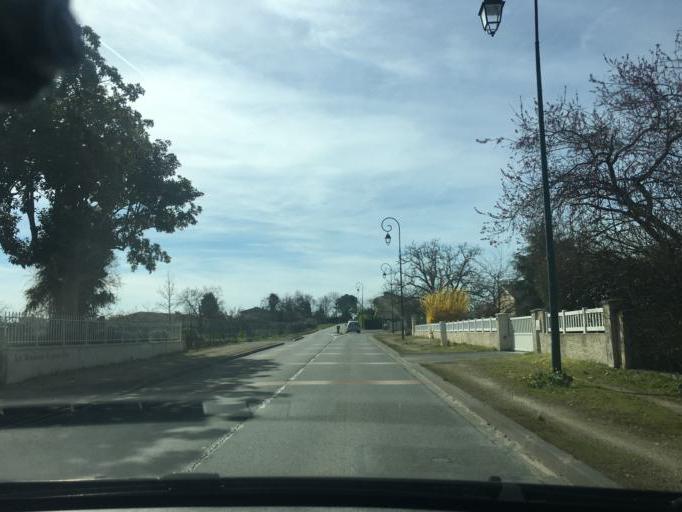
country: FR
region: Aquitaine
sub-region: Departement de la Gironde
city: Saint-Germain-du-Puch
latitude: 44.8543
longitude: -0.3242
